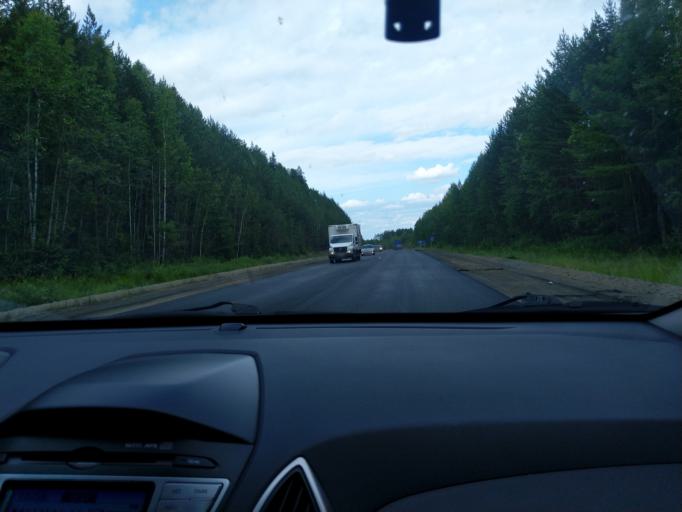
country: RU
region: Sverdlovsk
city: Nizhniy Tagil
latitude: 57.9204
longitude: 59.8456
